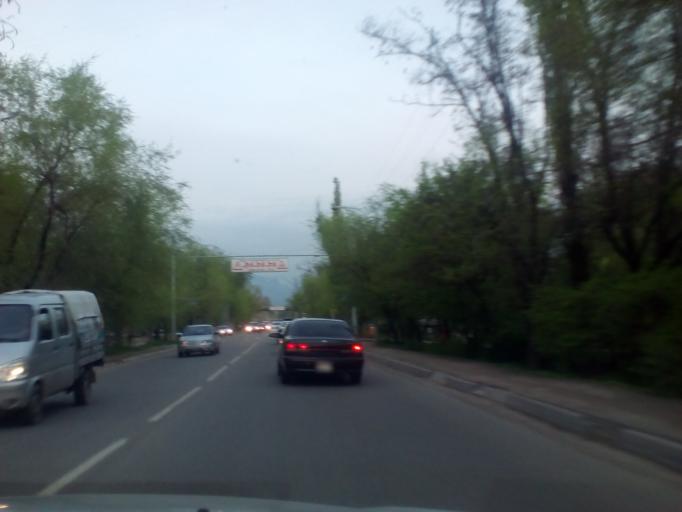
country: KZ
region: Almaty Qalasy
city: Almaty
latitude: 43.2355
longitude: 76.8247
